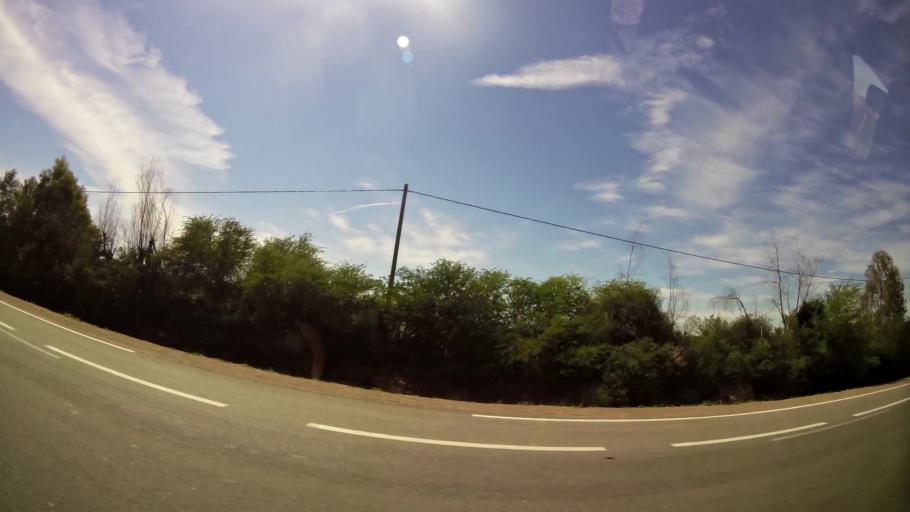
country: MA
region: Marrakech-Tensift-Al Haouz
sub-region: Marrakech
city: Marrakesh
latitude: 31.6570
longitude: -8.1053
